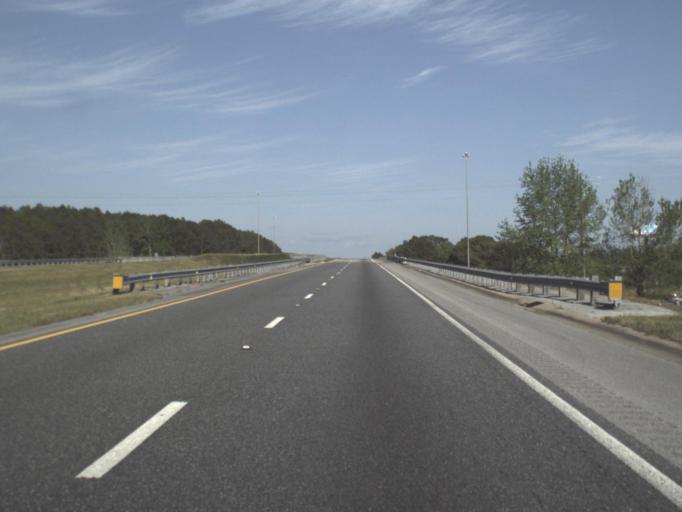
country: US
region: Florida
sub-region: Okaloosa County
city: Crestview
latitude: 30.7255
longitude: -86.5704
